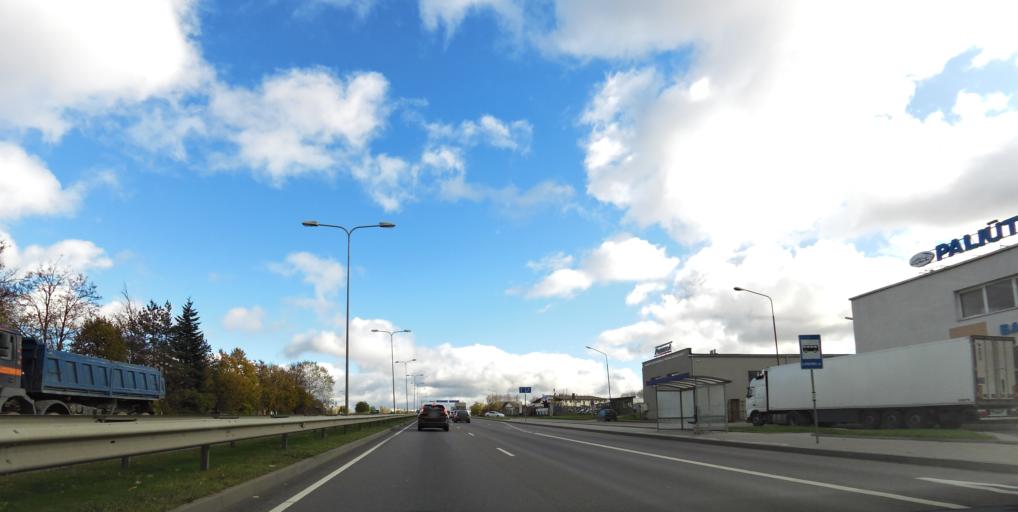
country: LT
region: Vilnius County
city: Rasos
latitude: 54.6551
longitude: 25.2980
